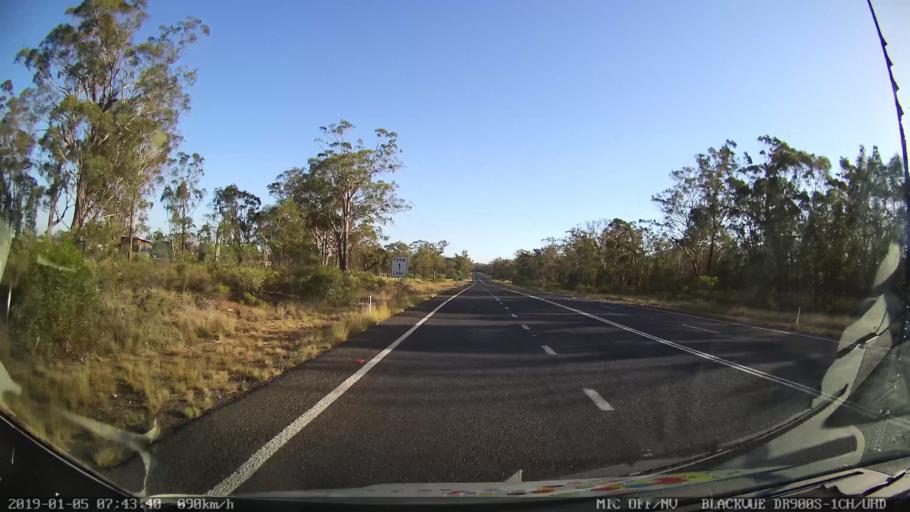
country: AU
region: New South Wales
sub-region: Gilgandra
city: Gilgandra
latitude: -31.8824
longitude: 148.6353
